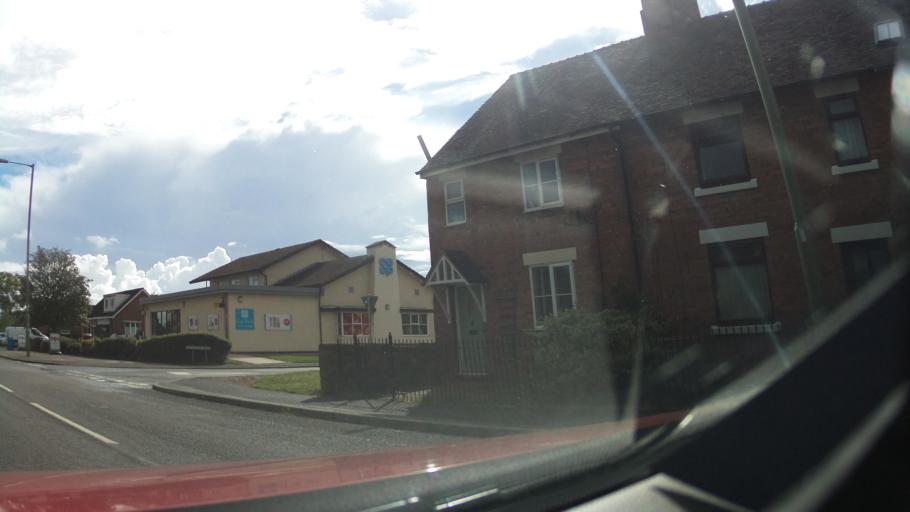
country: GB
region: England
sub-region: Shropshire
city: Shifnal
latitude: 52.6724
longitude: -2.3721
